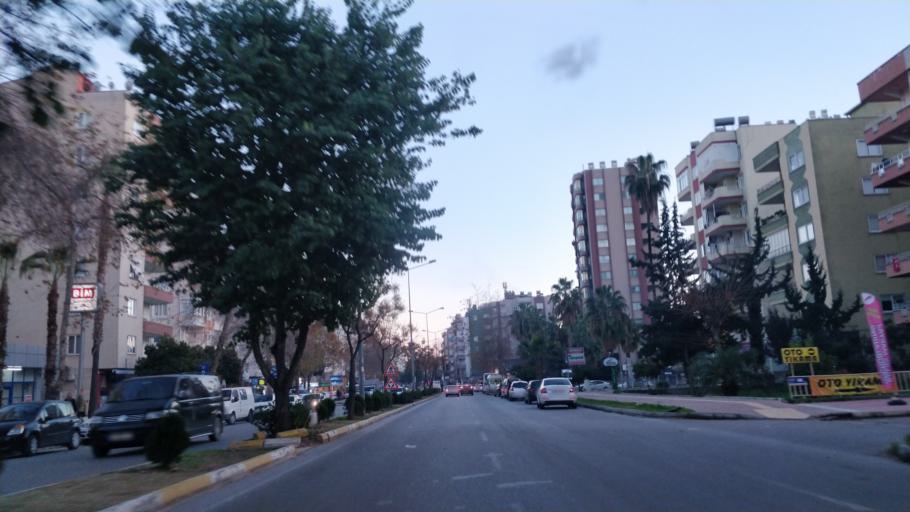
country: TR
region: Mersin
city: Mercin
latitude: 36.7880
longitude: 34.5933
